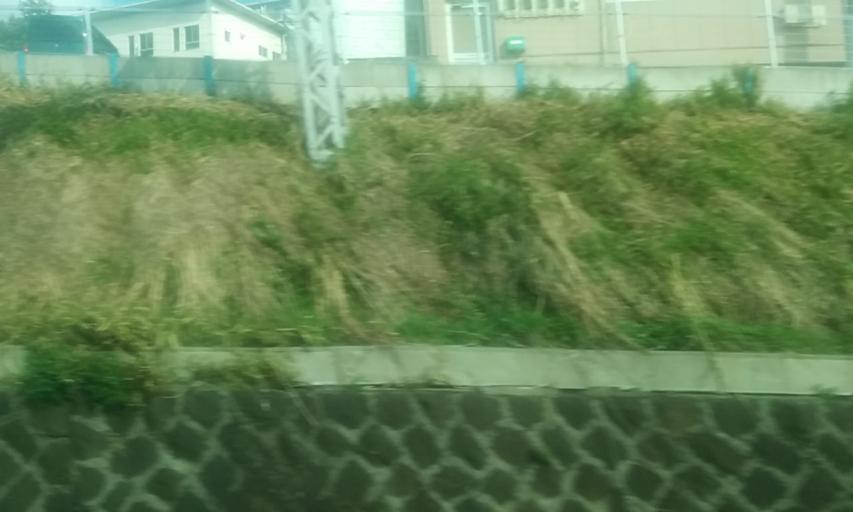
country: JP
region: Kanagawa
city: Yokohama
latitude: 35.4843
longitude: 139.6422
